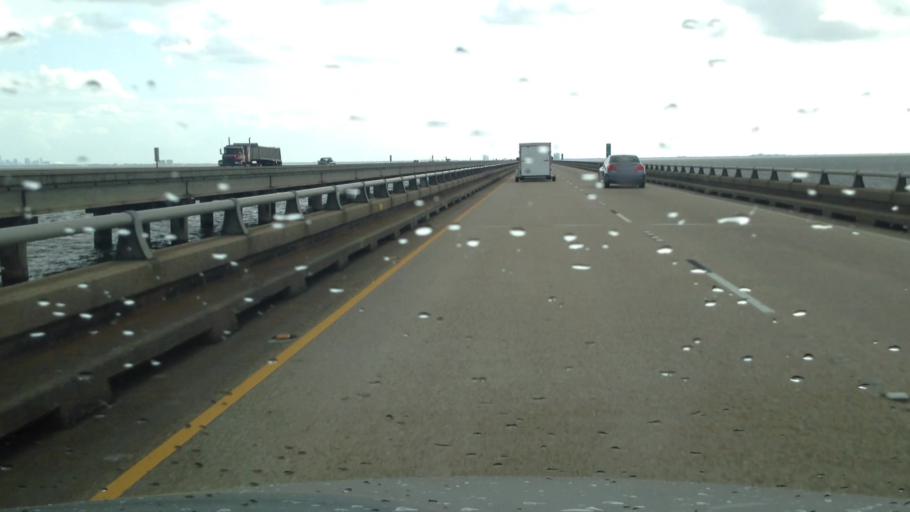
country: US
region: Louisiana
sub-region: Jefferson Parish
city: Metairie
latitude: 30.1087
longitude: -90.1389
